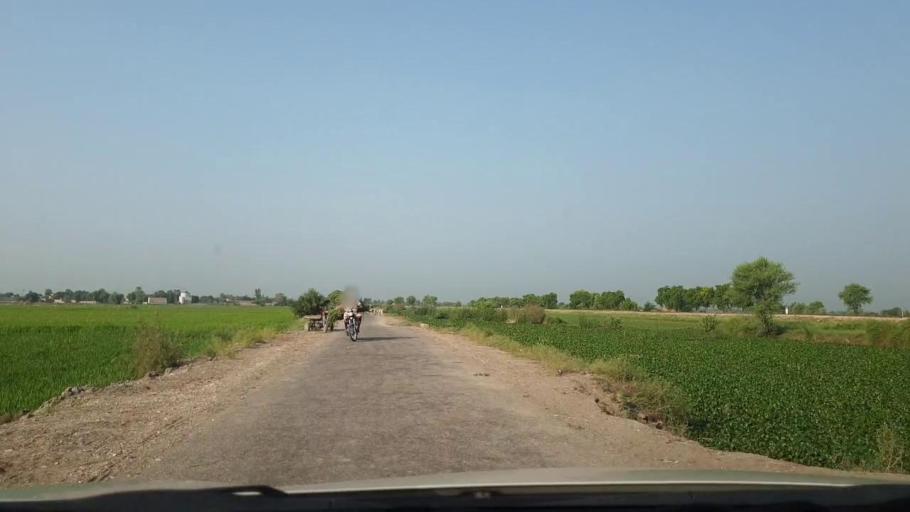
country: PK
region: Sindh
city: Larkana
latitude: 27.5103
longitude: 68.1835
